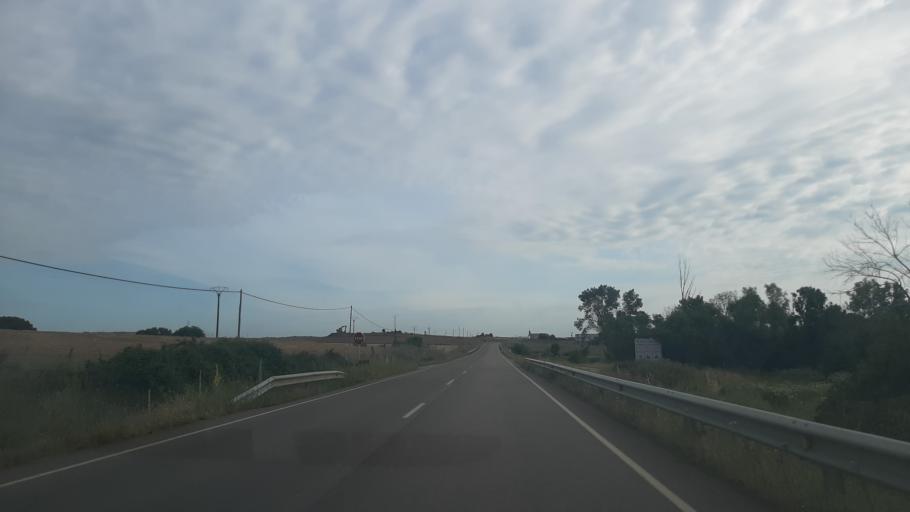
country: ES
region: Castille and Leon
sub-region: Provincia de Salamanca
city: Gallegos de Arganan
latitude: 40.6167
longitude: -6.7060
